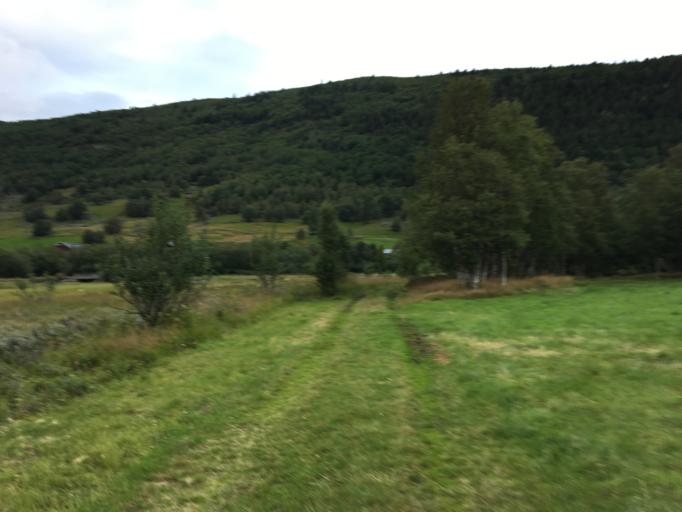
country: NO
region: Buskerud
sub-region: Hol
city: Hol
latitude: 60.6164
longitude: 8.2252
